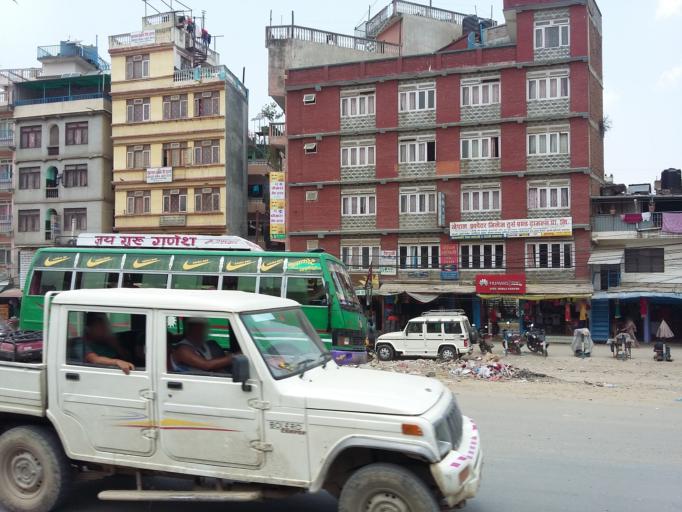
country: NP
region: Central Region
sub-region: Bagmati Zone
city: Kathmandu
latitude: 27.7350
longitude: 85.3097
